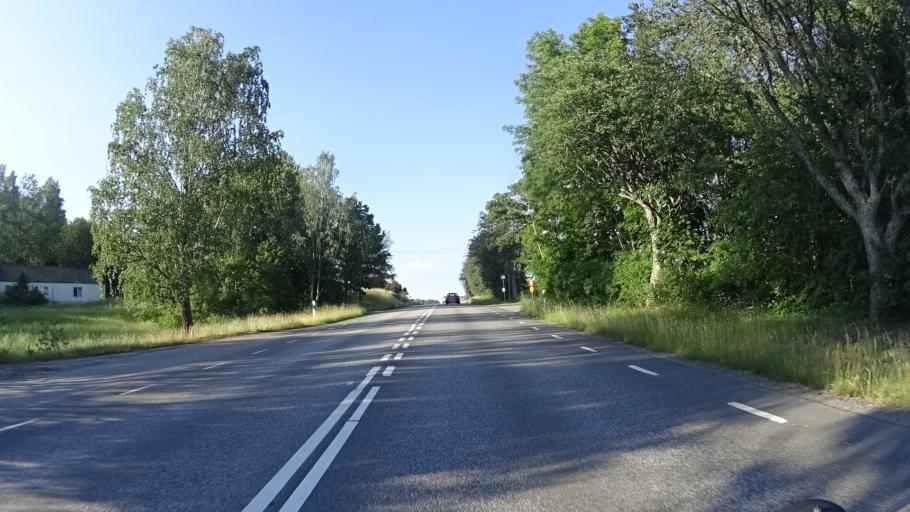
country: SE
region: Stockholm
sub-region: Sodertalje Kommun
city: Pershagen
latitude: 59.0882
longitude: 17.6125
